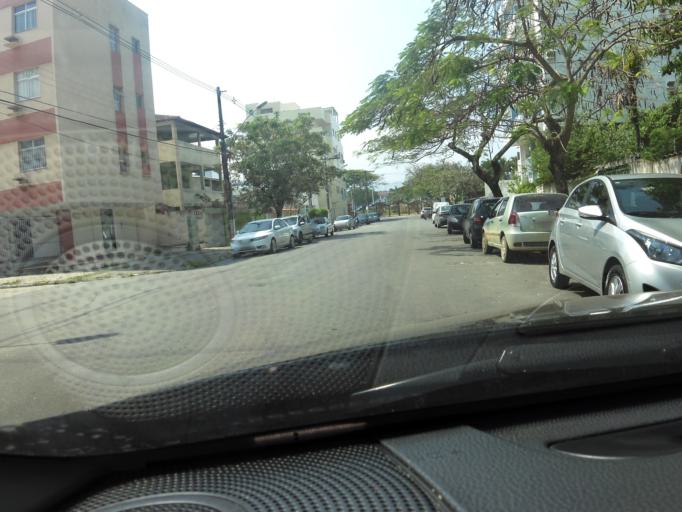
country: BR
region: Espirito Santo
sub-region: Guarapari
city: Guarapari
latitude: -20.6631
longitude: -40.4983
